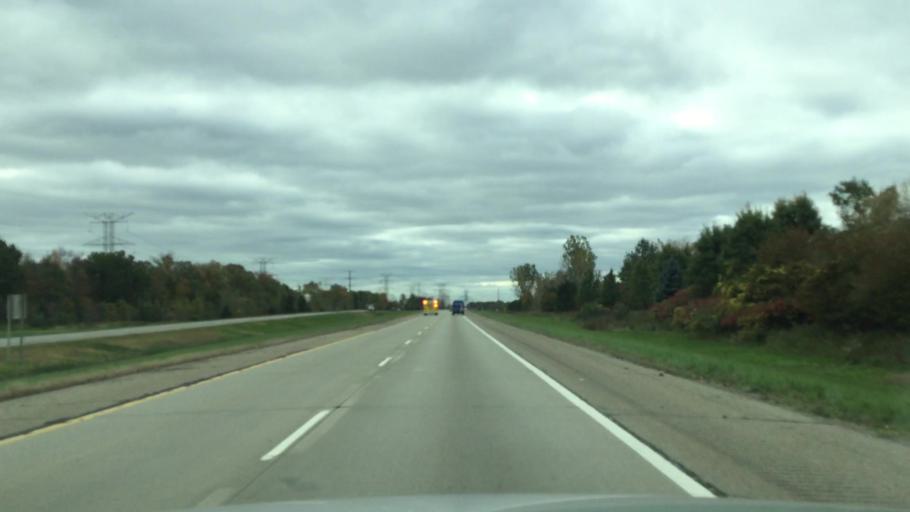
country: US
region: Michigan
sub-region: Macomb County
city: Romeo
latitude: 42.7690
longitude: -83.0094
